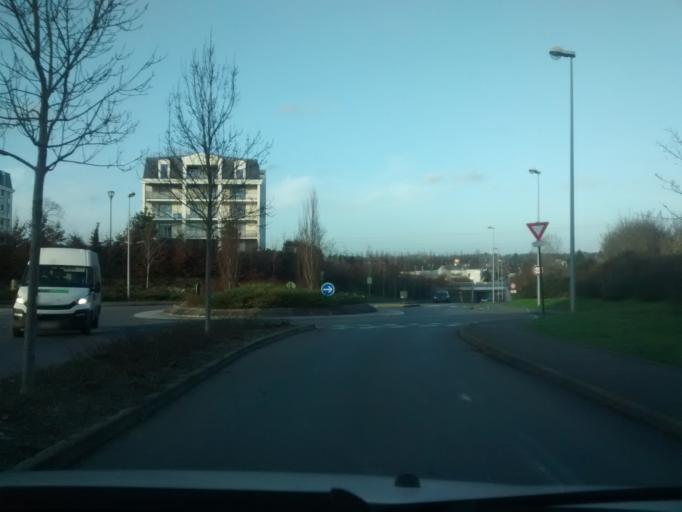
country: FR
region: Brittany
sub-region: Departement d'Ille-et-Vilaine
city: Cesson-Sevigne
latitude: 48.1095
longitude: -1.6090
